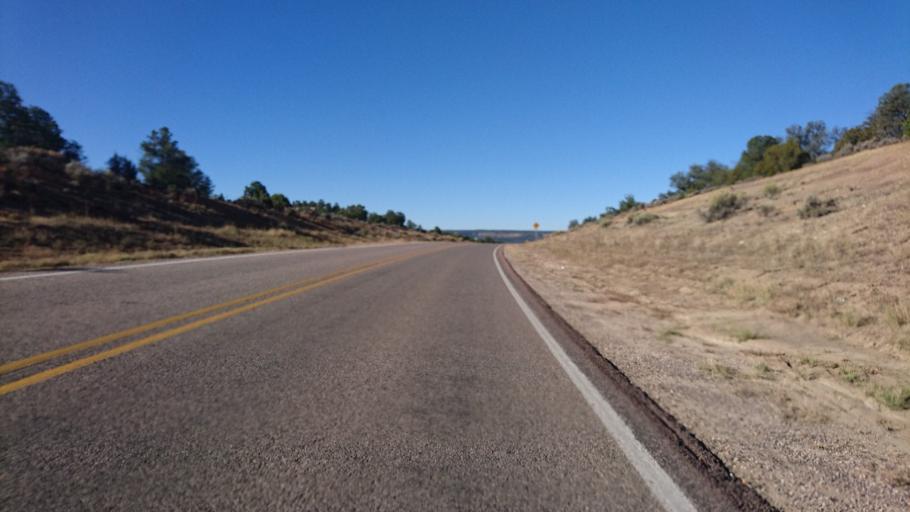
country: US
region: New Mexico
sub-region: McKinley County
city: Black Rock
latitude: 35.1239
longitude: -108.5369
